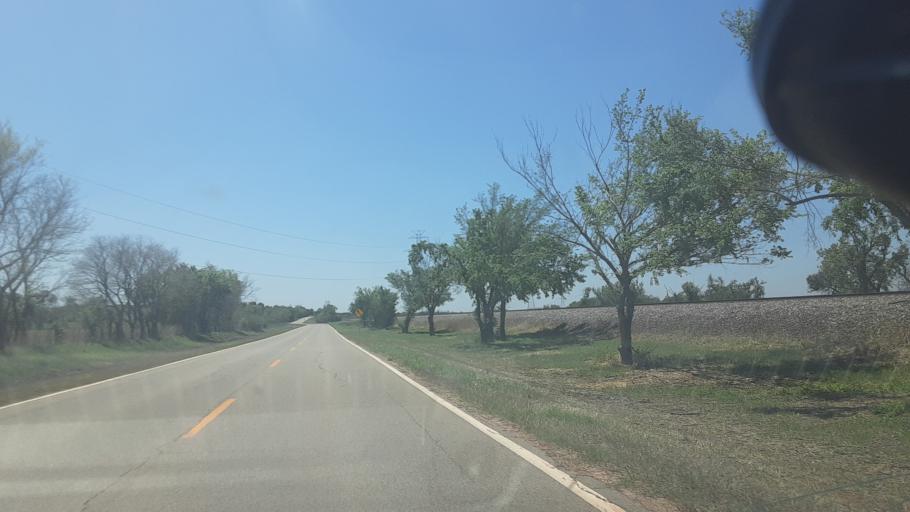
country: US
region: Oklahoma
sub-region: Logan County
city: Langston
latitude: 36.0966
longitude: -97.3947
